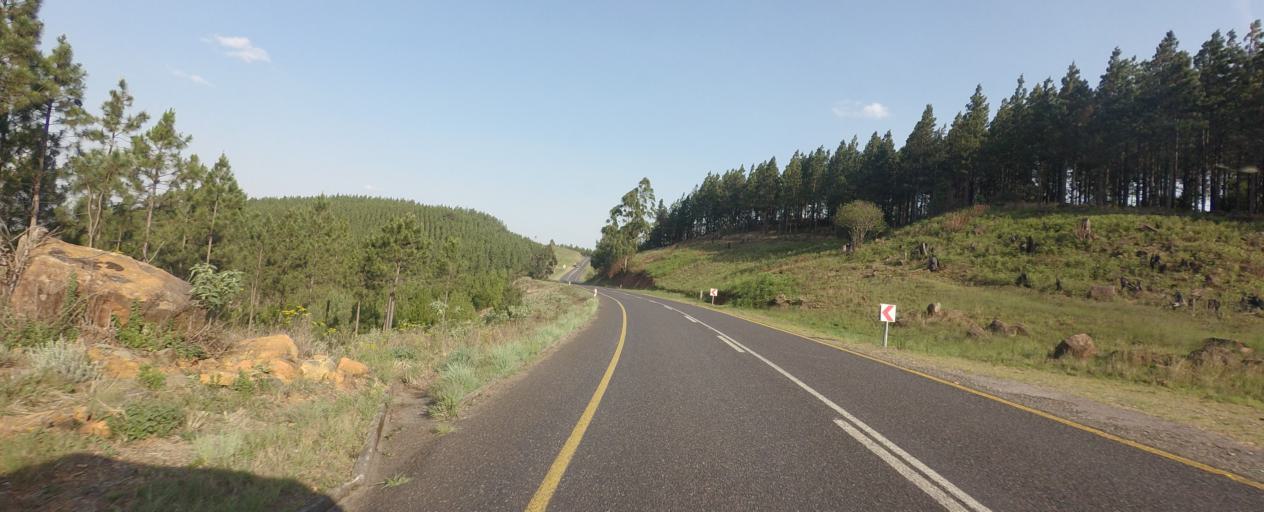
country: ZA
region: Mpumalanga
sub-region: Ehlanzeni District
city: Lydenburg
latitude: -25.1780
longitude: 30.6950
